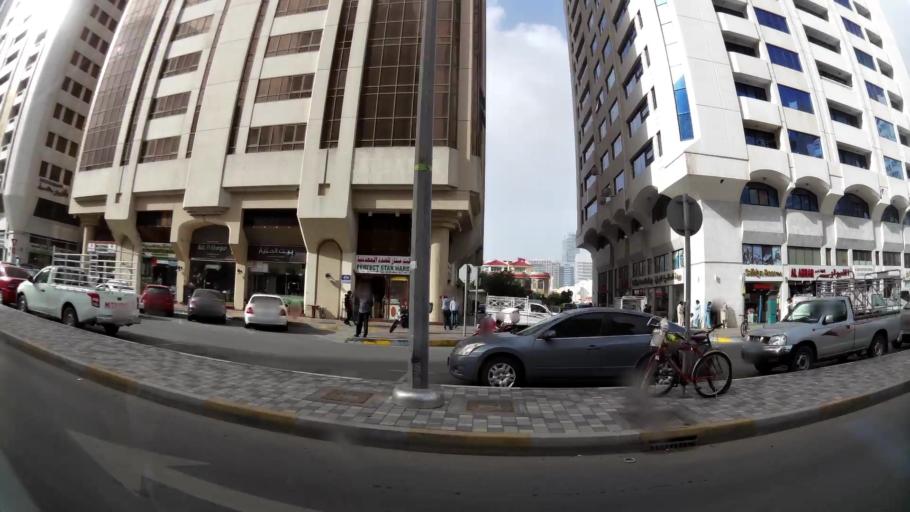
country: AE
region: Abu Dhabi
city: Abu Dhabi
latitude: 24.4878
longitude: 54.3714
